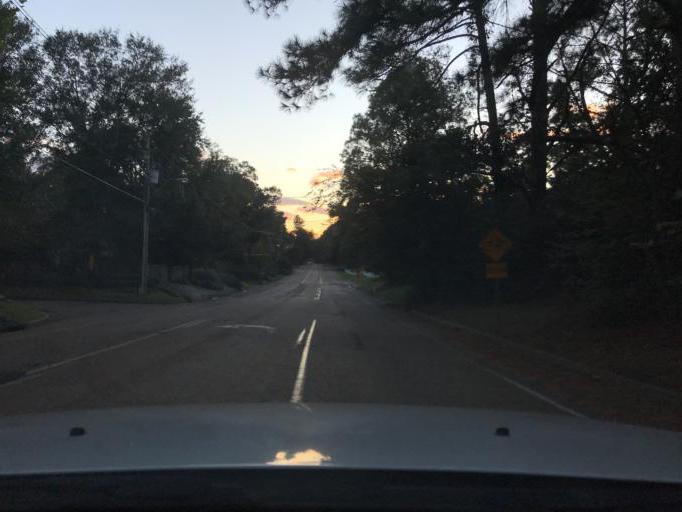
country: US
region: Mississippi
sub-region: Rankin County
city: Flowood
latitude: 32.3453
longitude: -90.1610
